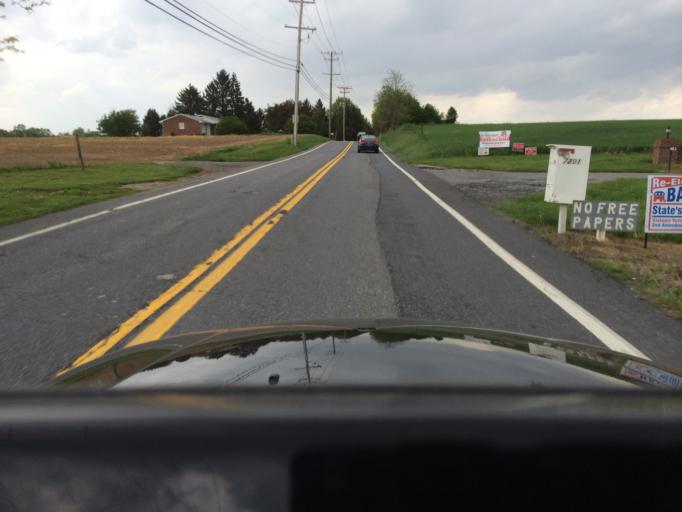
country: US
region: Maryland
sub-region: Carroll County
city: Sykesville
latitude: 39.3759
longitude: -77.0176
